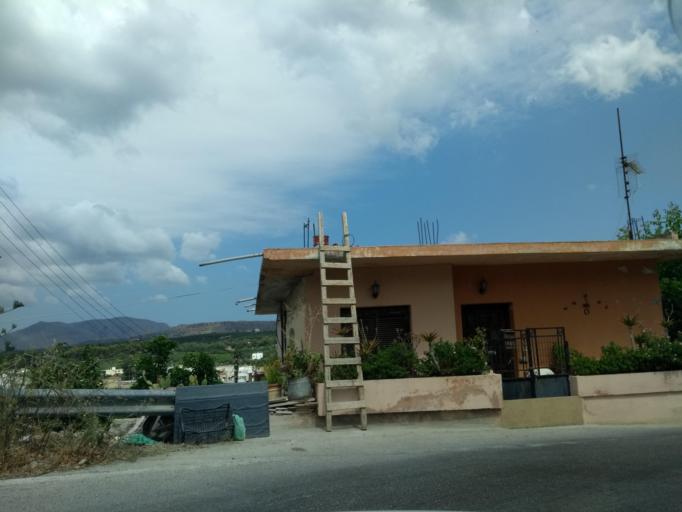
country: GR
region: Crete
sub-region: Nomos Chanias
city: Kalivai
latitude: 35.4488
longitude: 24.1743
